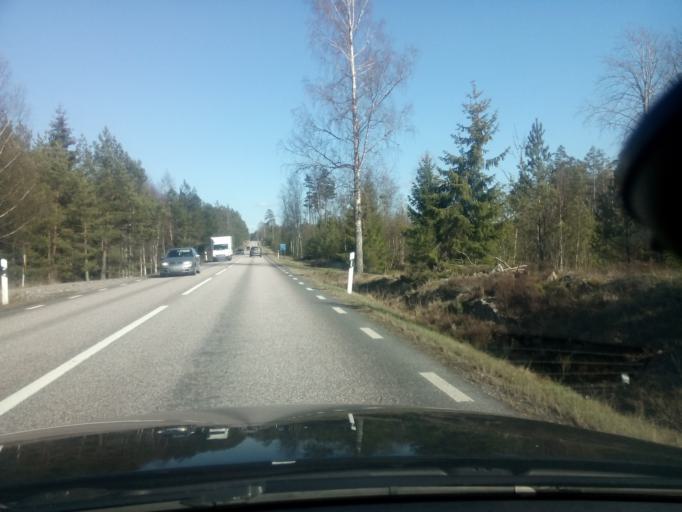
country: SE
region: Soedermanland
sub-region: Flens Kommun
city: Malmkoping
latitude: 59.2061
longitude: 16.8035
